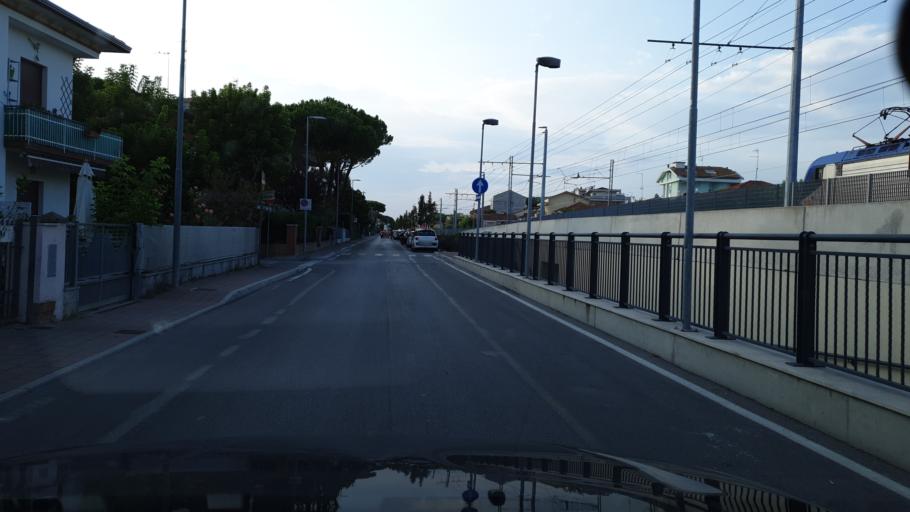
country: IT
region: Emilia-Romagna
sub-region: Provincia di Rimini
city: Riccione
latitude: 44.0073
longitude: 12.6480
